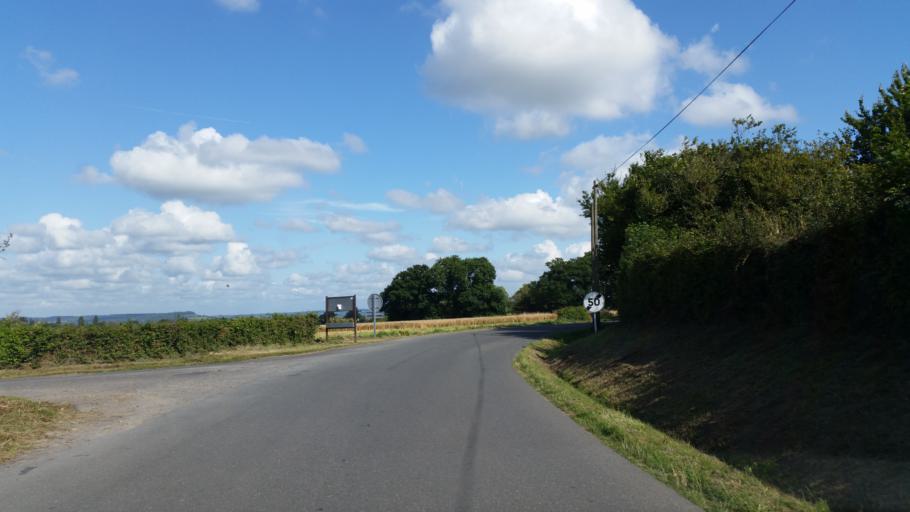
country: FR
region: Lower Normandy
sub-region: Departement du Calvados
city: Bavent
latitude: 49.2448
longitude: -0.2018
